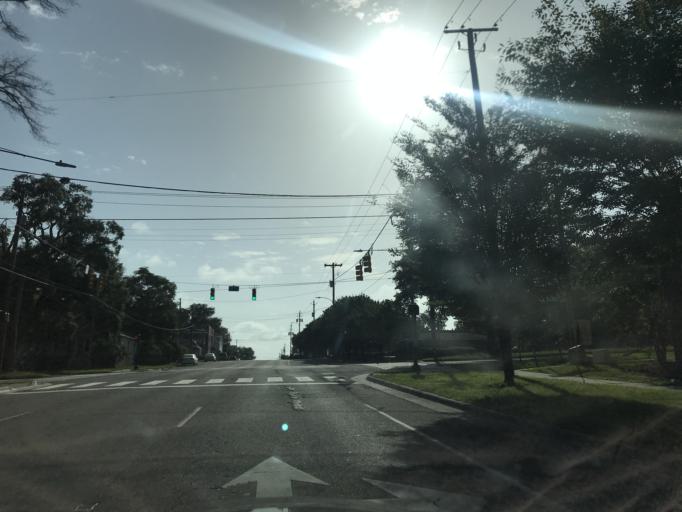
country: US
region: North Carolina
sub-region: New Hanover County
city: Wilmington
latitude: 34.2244
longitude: -77.9424
